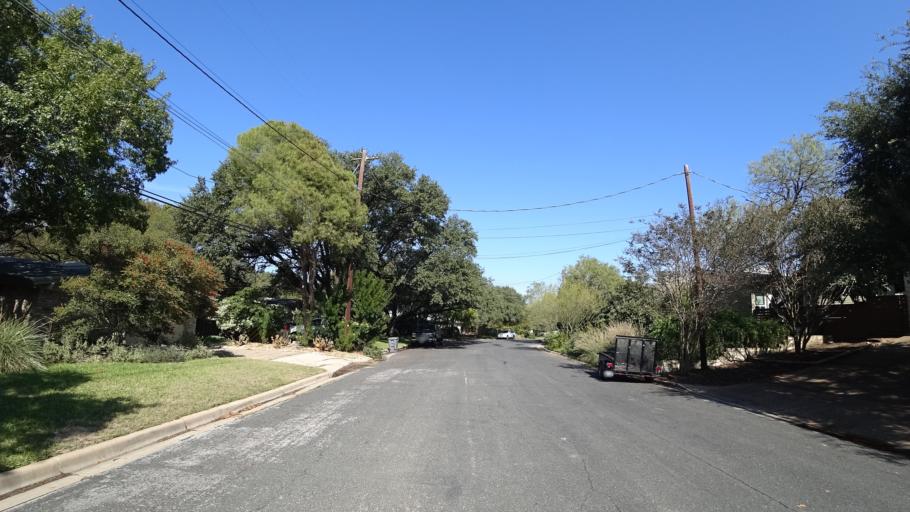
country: US
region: Texas
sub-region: Travis County
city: Austin
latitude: 30.2600
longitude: -97.7693
